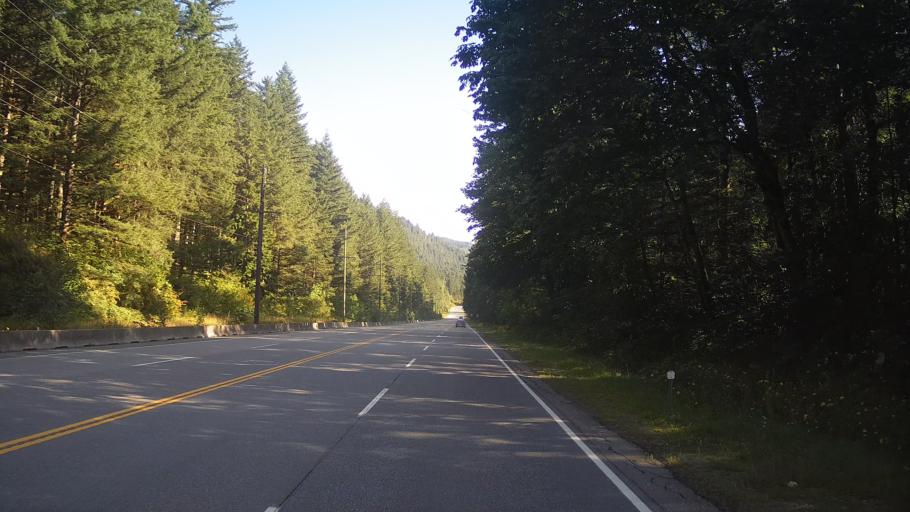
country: CA
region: British Columbia
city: Hope
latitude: 49.4510
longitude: -121.4372
